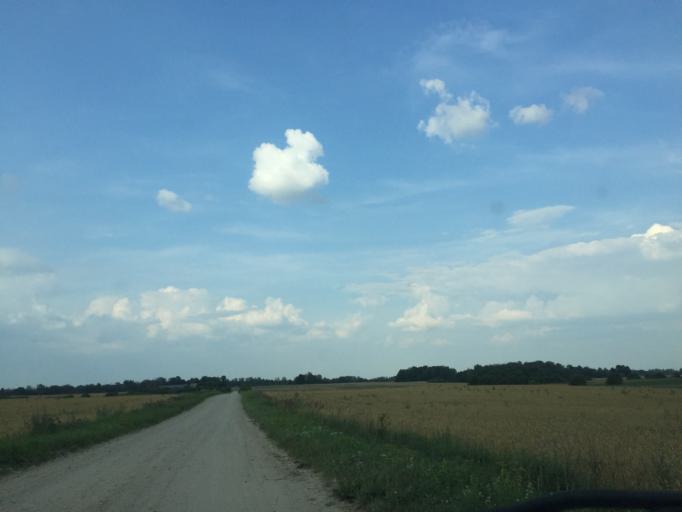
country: LT
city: Zagare
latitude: 56.4765
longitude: 23.1413
